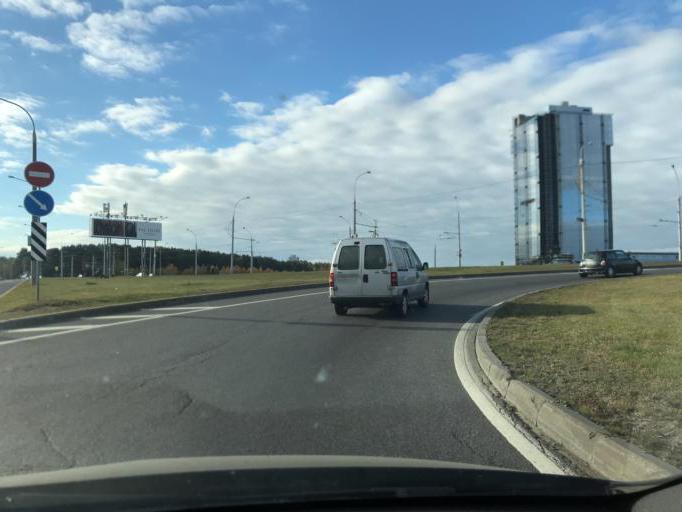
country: BY
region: Minsk
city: Borovlyany
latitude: 53.9395
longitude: 27.6714
